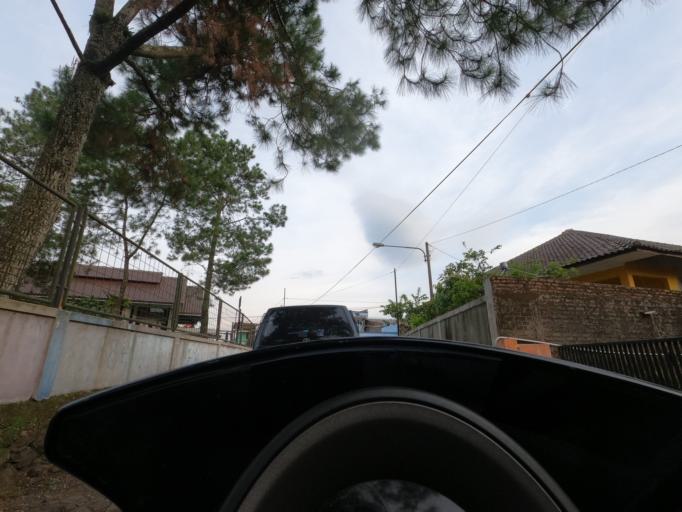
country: ID
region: West Java
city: Lembang
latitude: -6.7315
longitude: 107.6473
